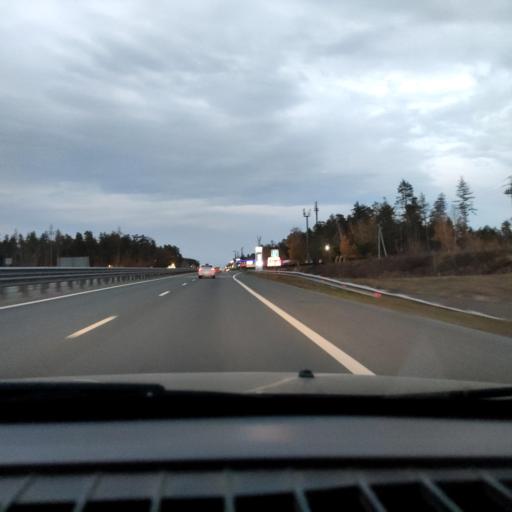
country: RU
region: Samara
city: Zhigulevsk
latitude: 53.5022
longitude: 49.5466
